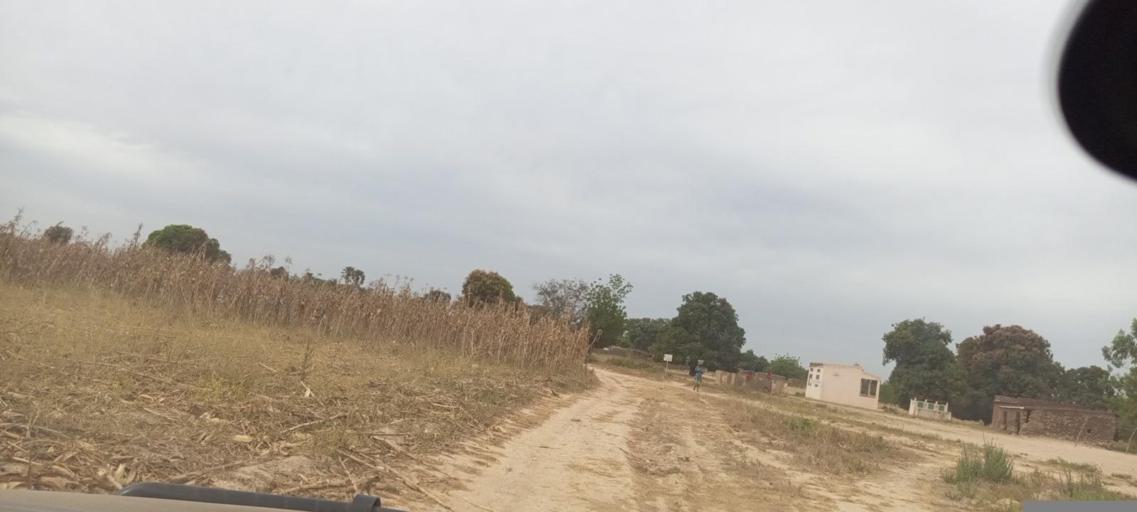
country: ML
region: Koulikoro
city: Kati
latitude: 12.7559
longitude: -8.3104
